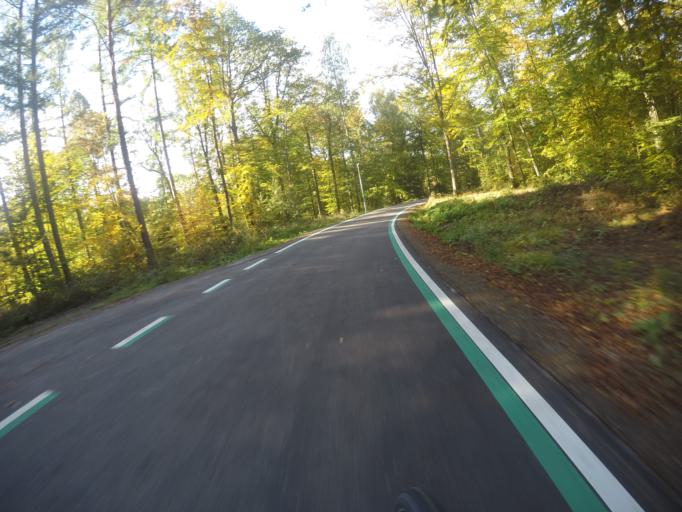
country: DE
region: Baden-Wuerttemberg
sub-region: Regierungsbezirk Stuttgart
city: Schonaich
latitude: 48.7021
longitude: 9.0621
